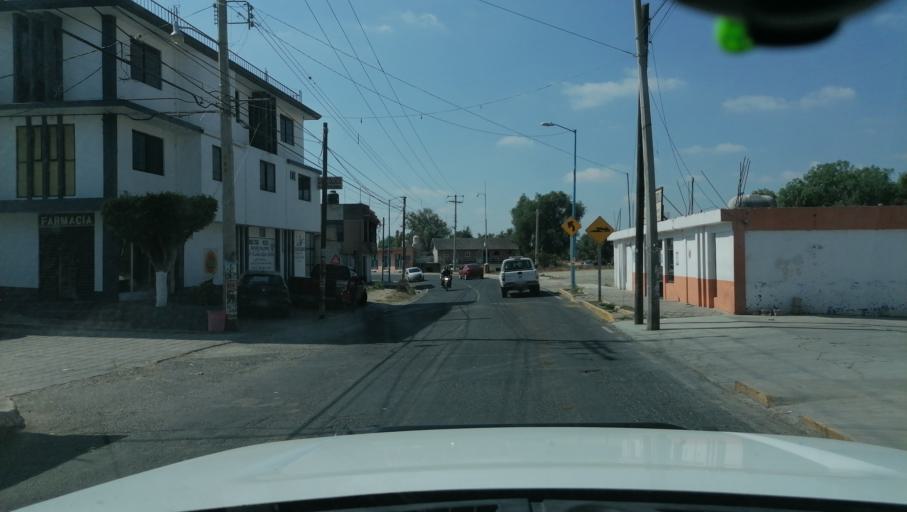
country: MX
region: Tlaxcala
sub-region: Tetlatlahuca
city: Tetlatlahuca
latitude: 19.2348
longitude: -98.3010
